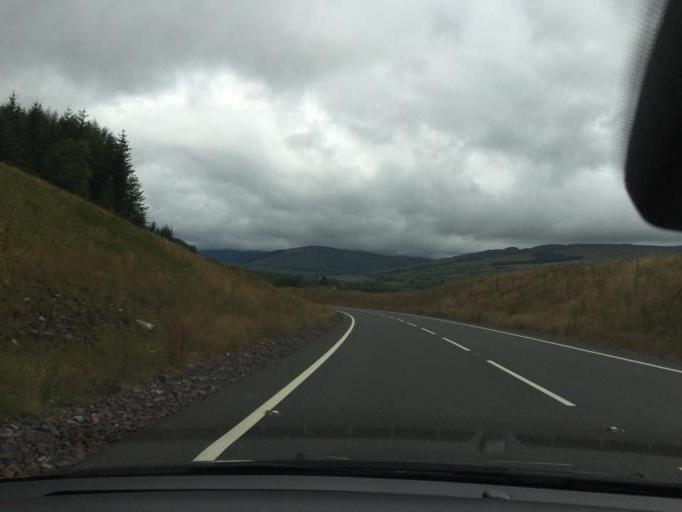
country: GB
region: Scotland
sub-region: Argyll and Bute
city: Garelochhead
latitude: 56.3915
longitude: -4.6210
